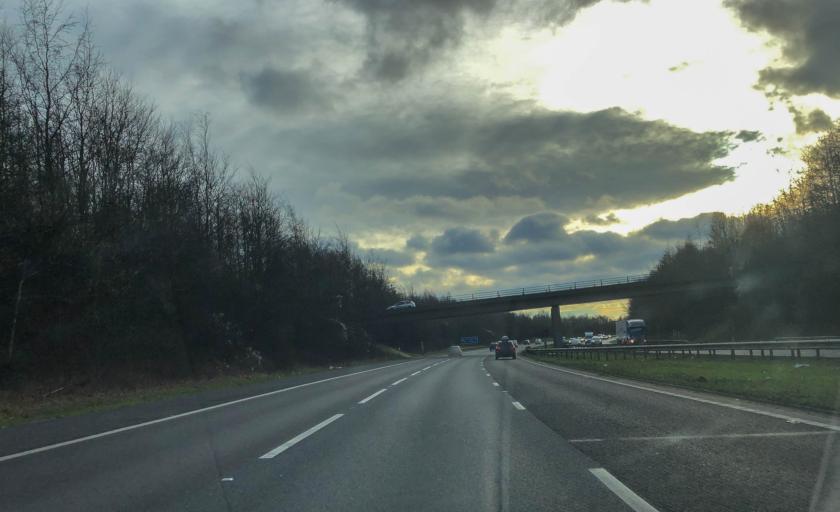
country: GB
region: England
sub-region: Kent
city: Shoreham
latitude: 51.3101
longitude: 0.1602
